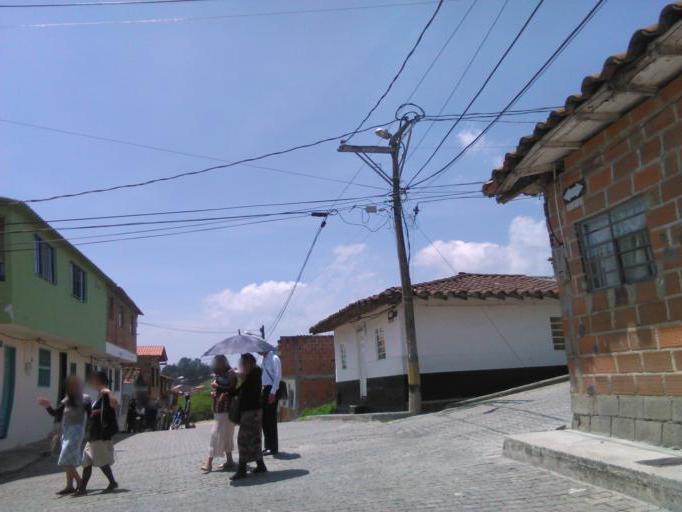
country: CO
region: Antioquia
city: La Union
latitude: 5.9727
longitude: -75.3631
